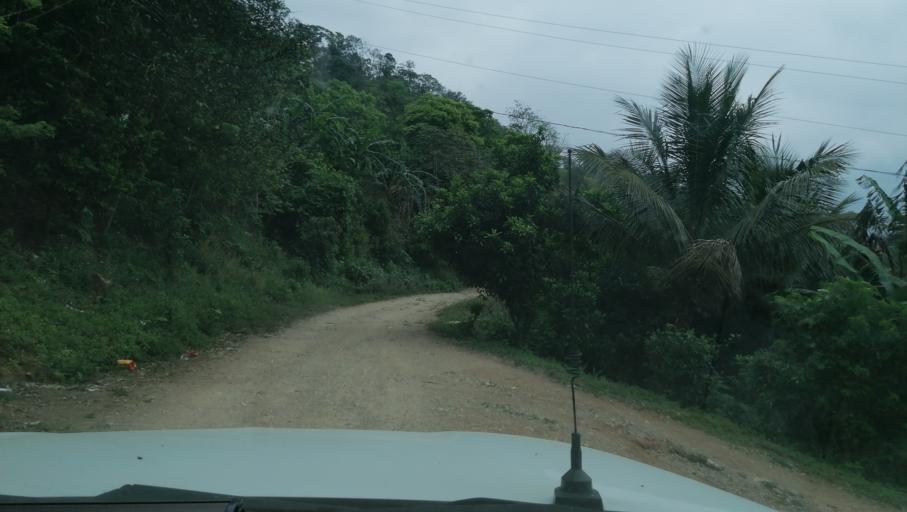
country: MX
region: Chiapas
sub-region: Francisco Leon
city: San Miguel la Sardina
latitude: 17.3442
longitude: -93.3112
